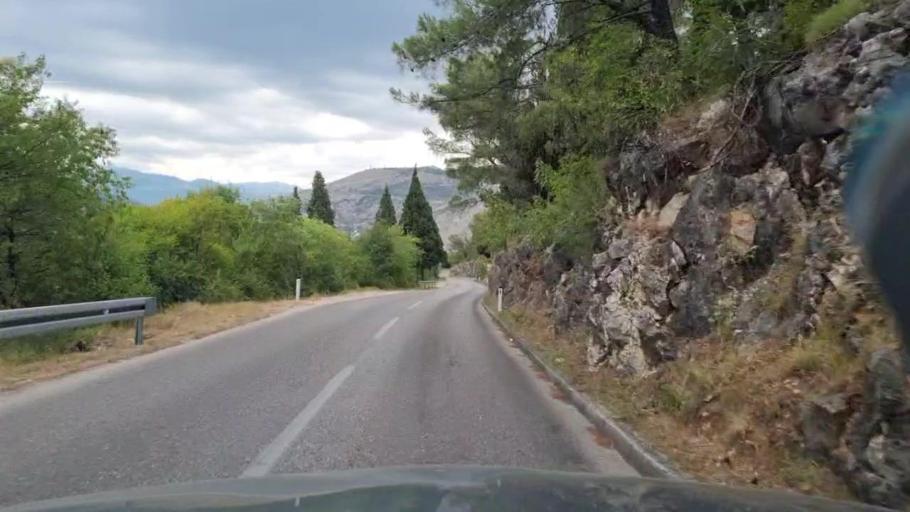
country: BA
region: Federation of Bosnia and Herzegovina
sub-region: Hercegovacko-Bosanski Kanton
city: Mostar
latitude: 43.3317
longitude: 17.7996
